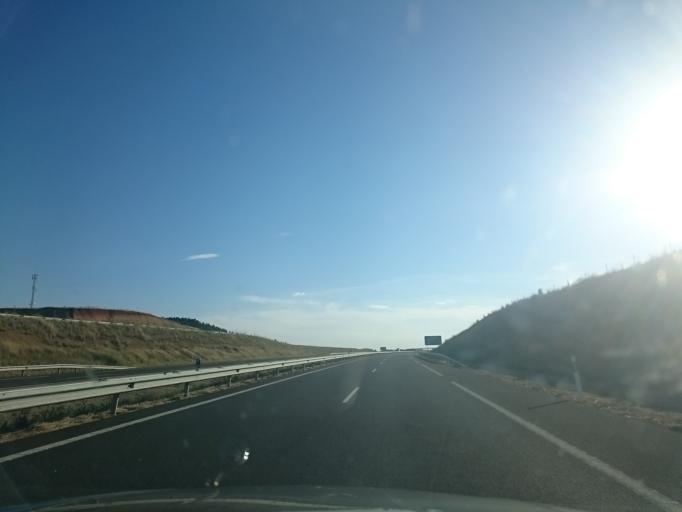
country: ES
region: Castille and Leon
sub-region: Provincia de Palencia
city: Villaherreros
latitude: 42.3870
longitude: -4.4837
